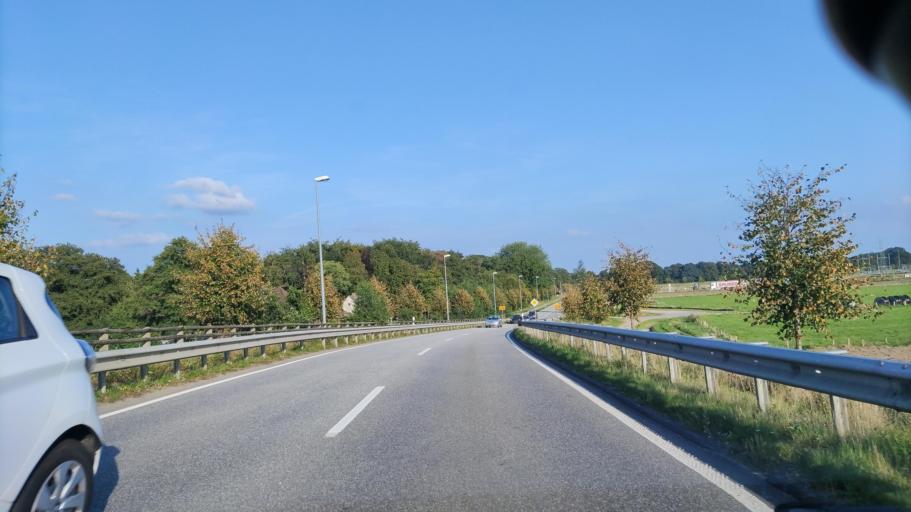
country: DE
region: Schleswig-Holstein
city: Bad Bramstedt
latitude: 53.9164
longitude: 9.8915
